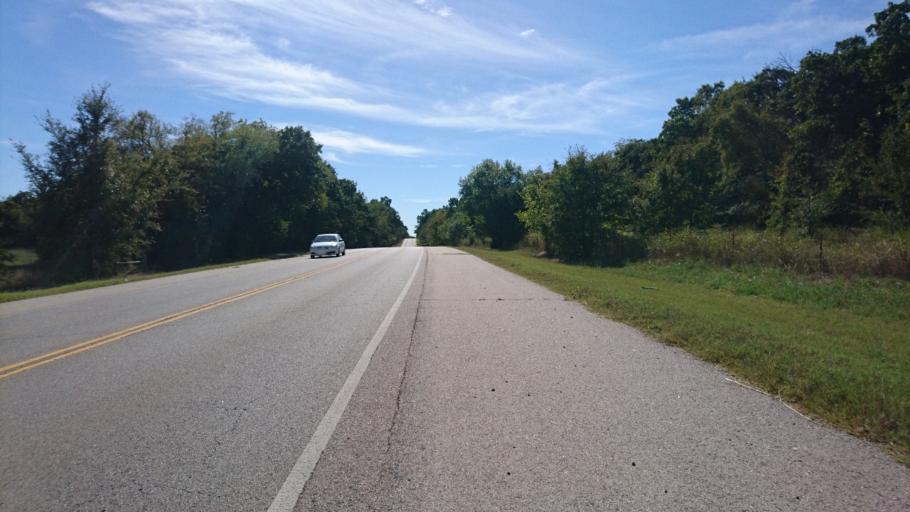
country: US
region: Oklahoma
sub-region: Lincoln County
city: Stroud
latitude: 35.7348
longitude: -96.7215
